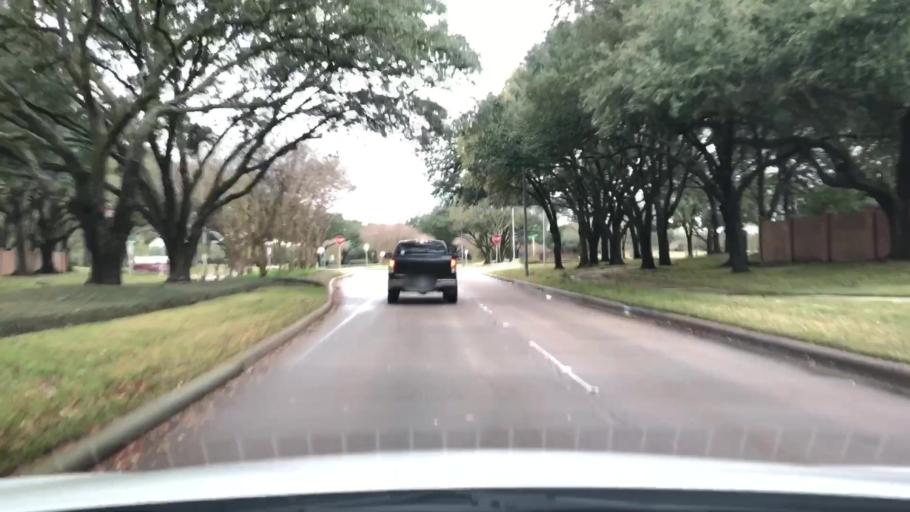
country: US
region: Texas
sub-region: Fort Bend County
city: Cinco Ranch
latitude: 29.7413
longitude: -95.7570
